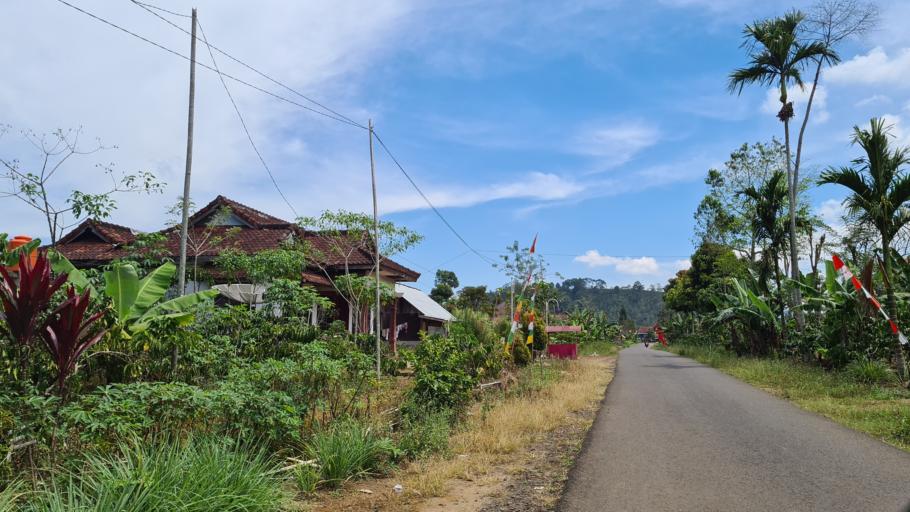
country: ID
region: Lampung
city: Kenali
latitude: -5.0958
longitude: 104.4263
